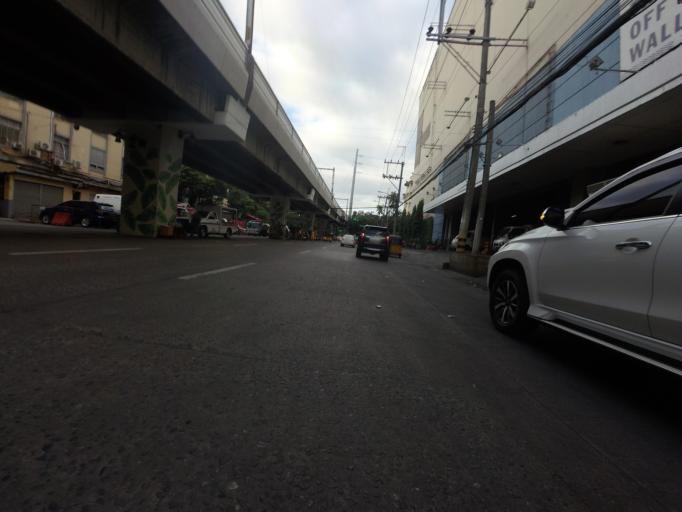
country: PH
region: Metro Manila
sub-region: City of Manila
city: Quiapo
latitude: 14.5896
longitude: 120.9822
